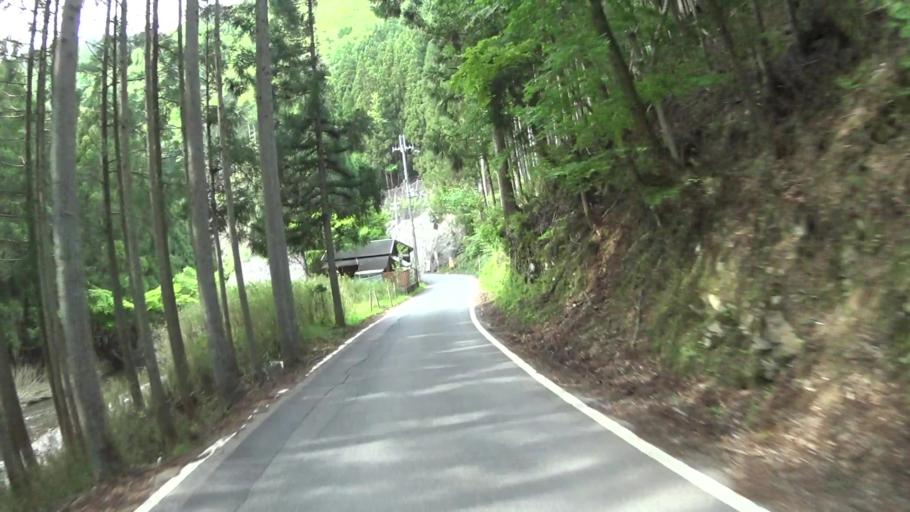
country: JP
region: Kyoto
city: Kameoka
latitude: 35.1196
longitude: 135.6177
